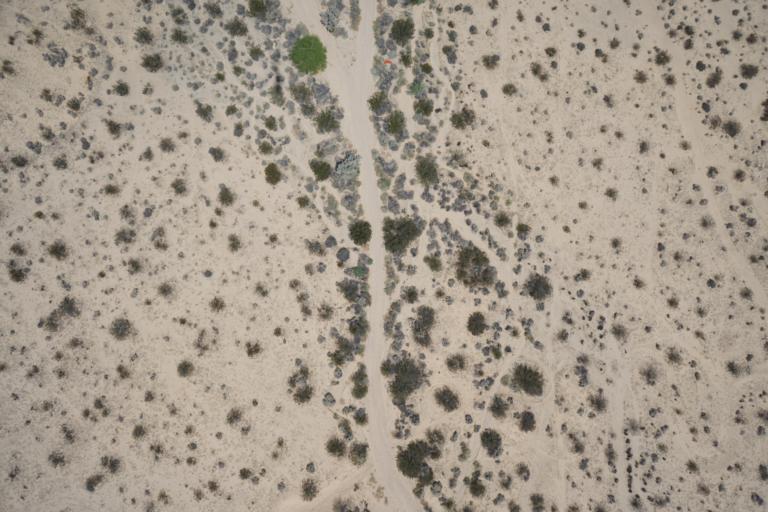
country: US
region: California
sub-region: San Bernardino County
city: Twentynine Palms
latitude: 34.1586
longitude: -116.0455
